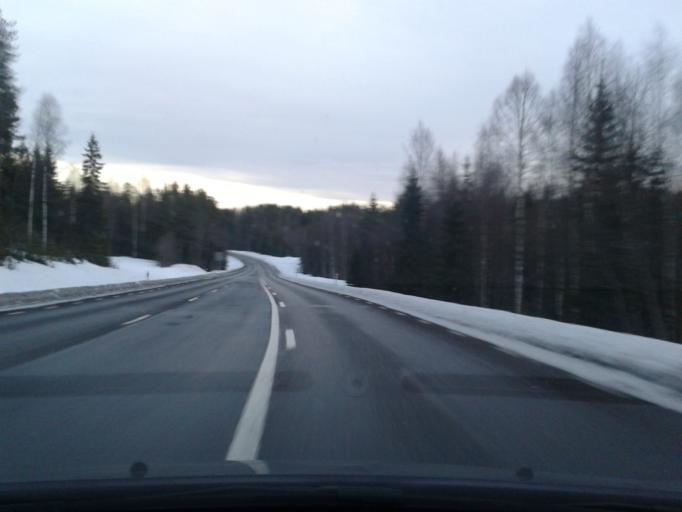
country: SE
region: Vaesternorrland
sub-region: Kramfors Kommun
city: Bollstabruk
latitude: 63.1033
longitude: 17.5102
